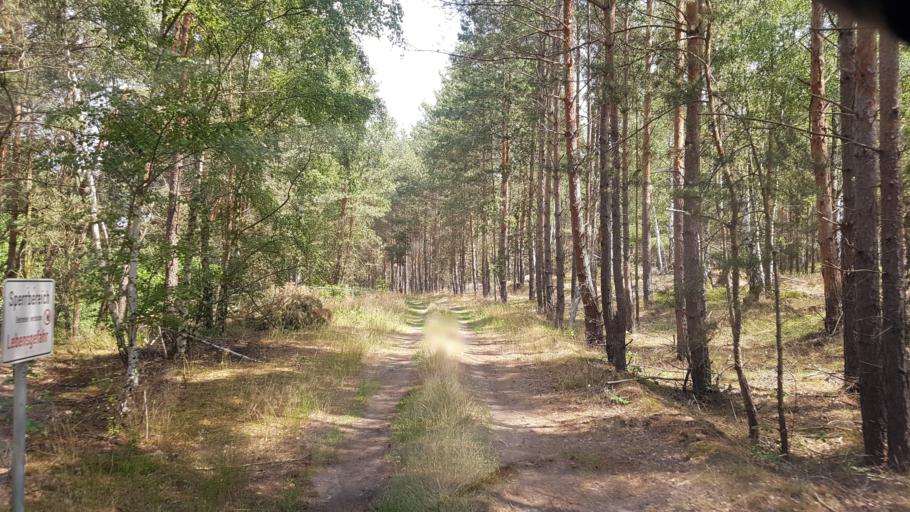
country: DE
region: Brandenburg
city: Crinitz
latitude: 51.7540
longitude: 13.8444
